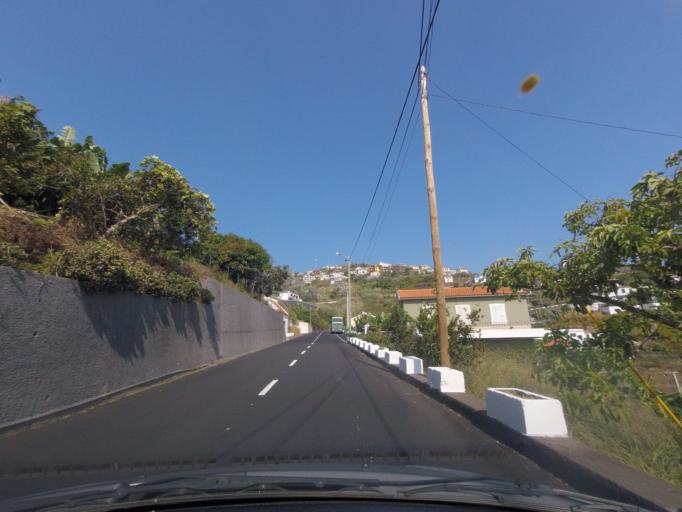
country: PT
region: Madeira
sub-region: Ribeira Brava
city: Campanario
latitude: 32.6691
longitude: -17.0546
